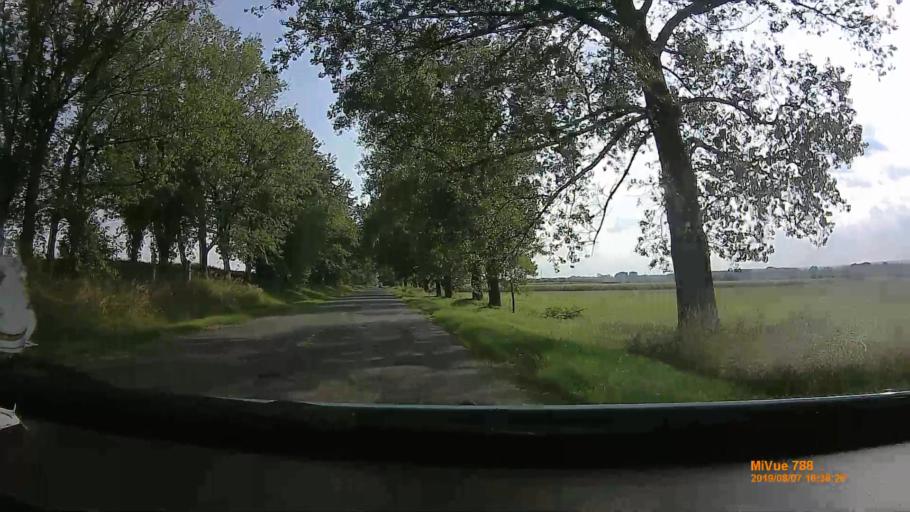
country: HU
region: Borsod-Abauj-Zemplen
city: Gonc
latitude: 48.4033
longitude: 21.2288
